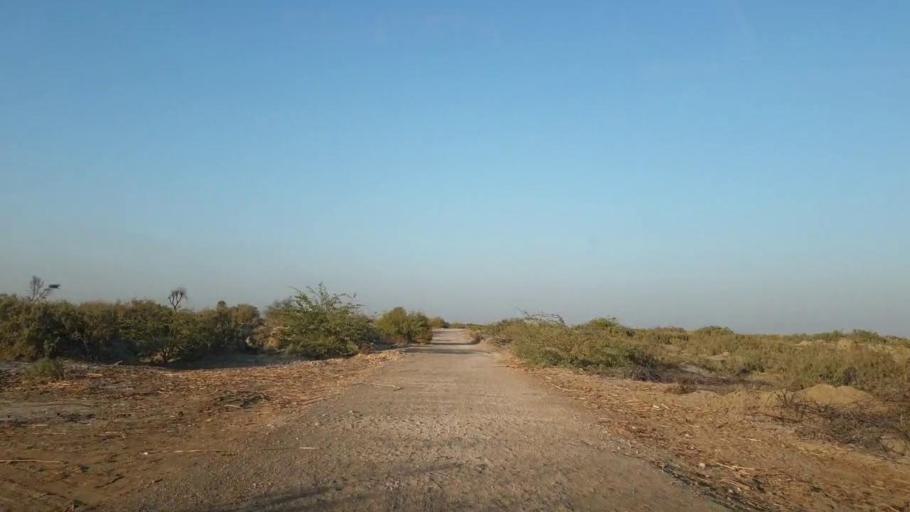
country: PK
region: Sindh
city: Mirpur Khas
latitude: 25.6788
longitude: 69.0477
